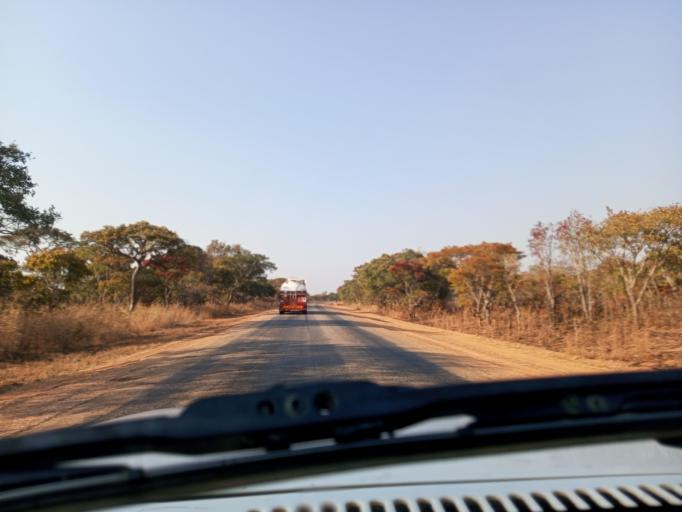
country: ZM
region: Northern
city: Mpika
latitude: -12.3648
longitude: 31.1039
